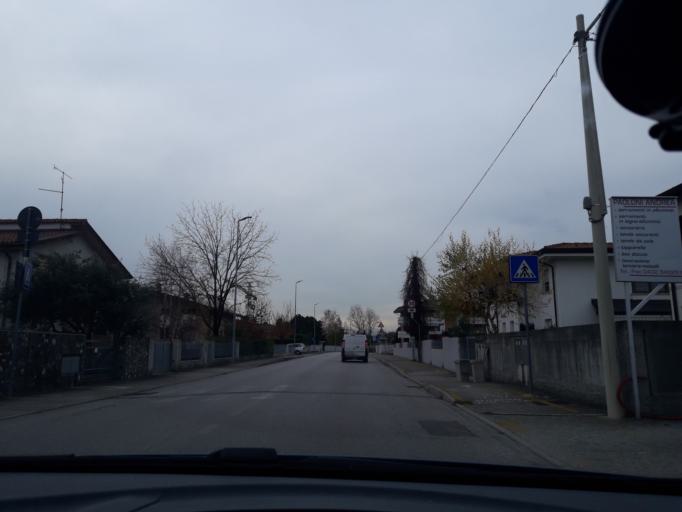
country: IT
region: Friuli Venezia Giulia
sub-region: Provincia di Udine
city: Colugna
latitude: 46.0887
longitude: 13.1989
